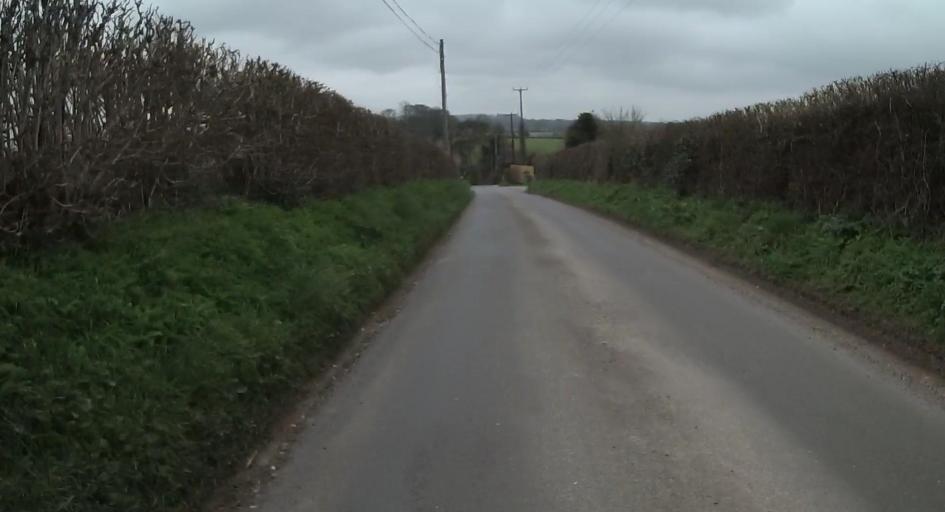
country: GB
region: England
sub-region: Hampshire
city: Four Marks
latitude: 51.0874
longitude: -1.0980
